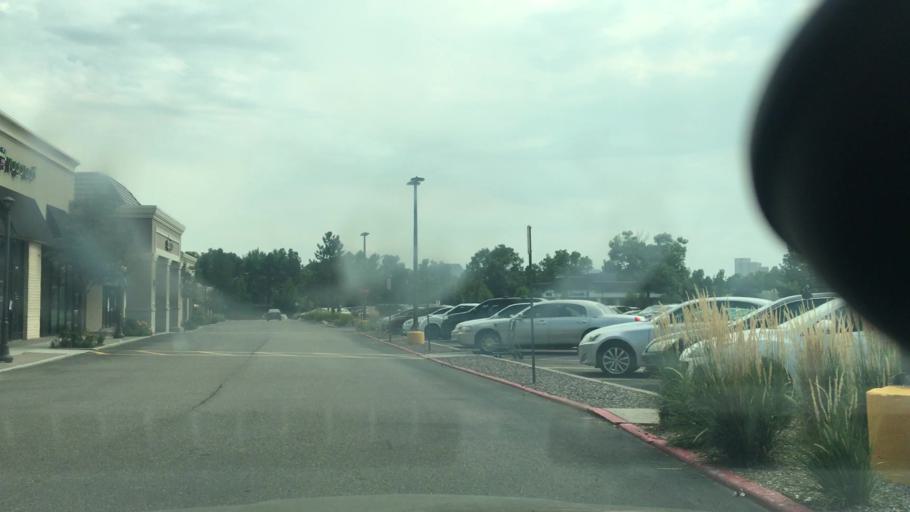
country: US
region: Colorado
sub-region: Arapahoe County
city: Castlewood
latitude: 39.6257
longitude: -104.8836
